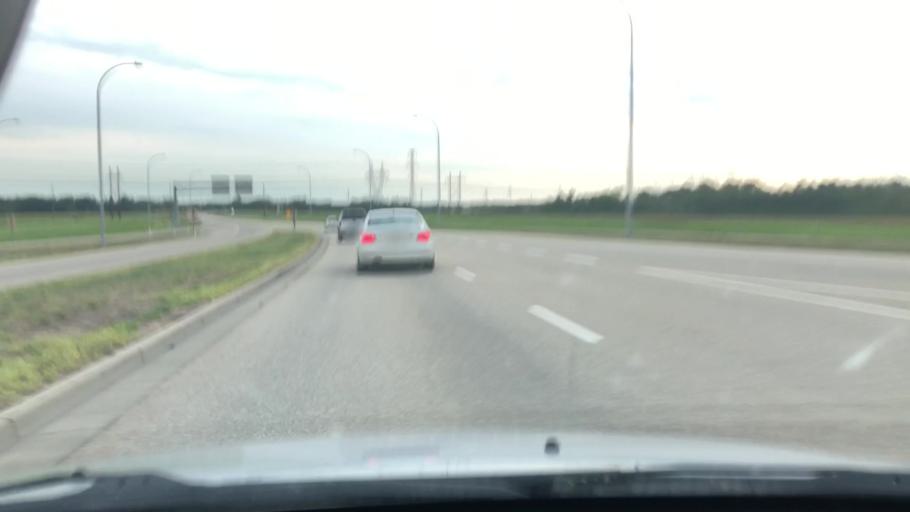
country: CA
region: Alberta
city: Devon
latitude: 53.4648
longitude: -113.6346
